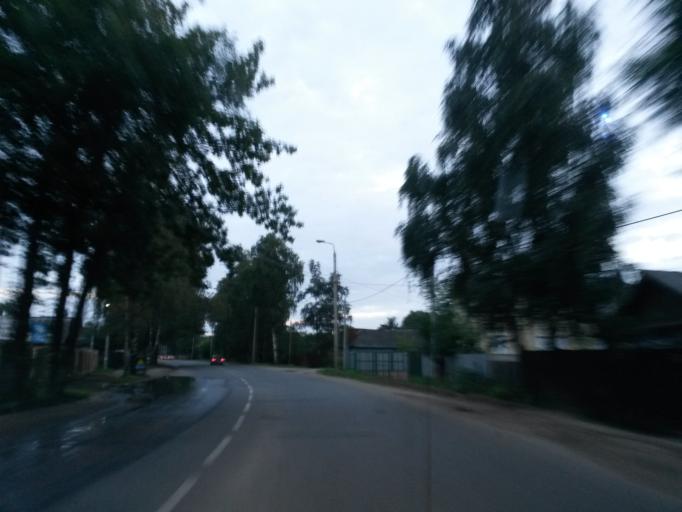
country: RU
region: Jaroslavl
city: Yaroslavl
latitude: 57.6508
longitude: 39.9062
